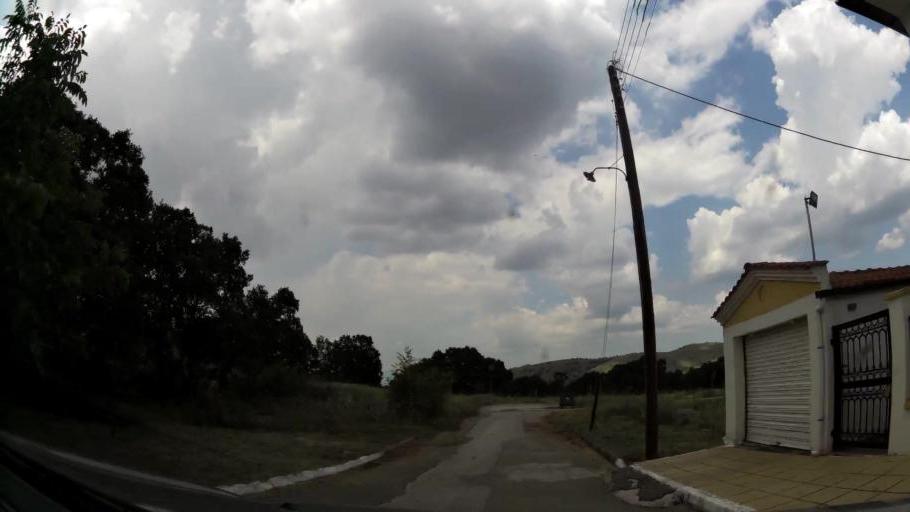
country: GR
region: West Macedonia
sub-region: Nomos Kozanis
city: Koila
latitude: 40.3284
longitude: 21.8212
